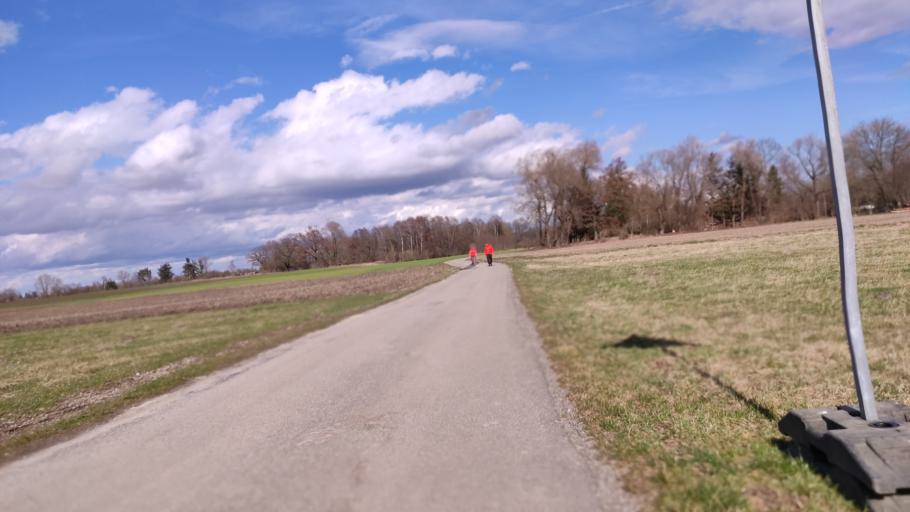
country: DE
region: Bavaria
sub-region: Upper Bavaria
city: Emmering
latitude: 48.1870
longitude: 11.2933
